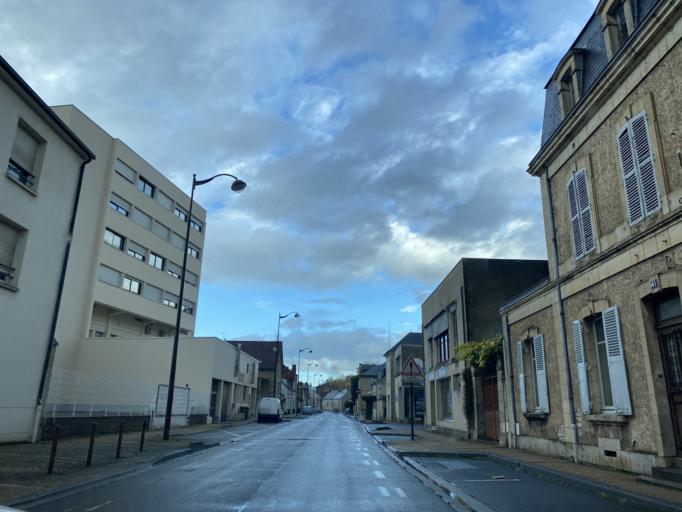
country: FR
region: Centre
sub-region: Departement du Cher
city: Bourges
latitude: 47.0750
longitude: 2.3903
